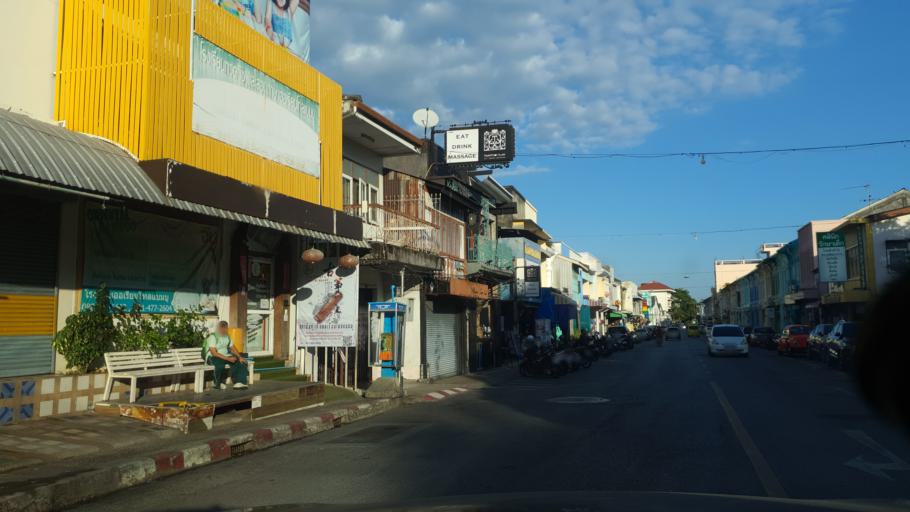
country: TH
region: Phuket
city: Ban Talat Nua
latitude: 7.8866
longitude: 98.3855
